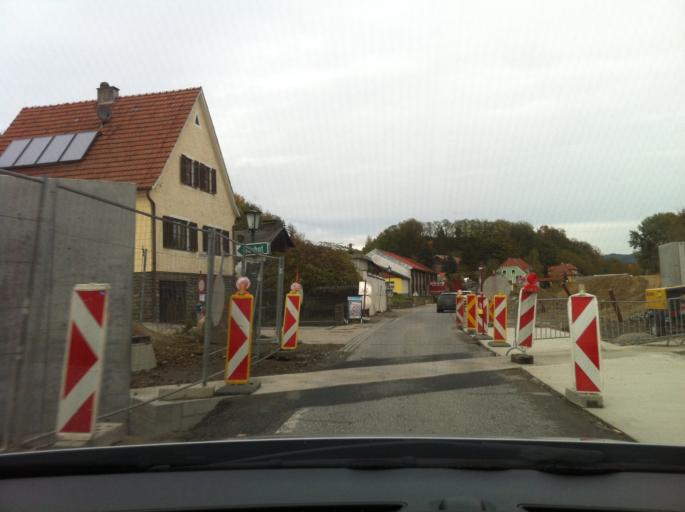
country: AT
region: Lower Austria
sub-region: Politischer Bezirk Melk
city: Melk
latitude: 48.2357
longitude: 15.3238
